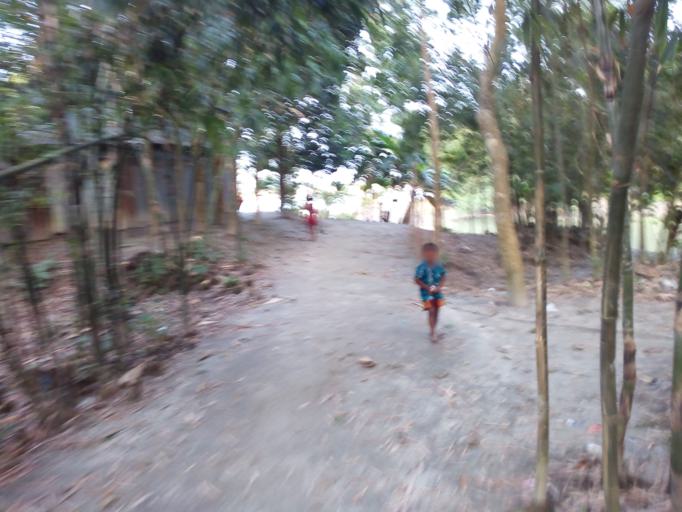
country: BD
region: Rangpur Division
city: Nageswari
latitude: 25.8700
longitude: 89.7866
